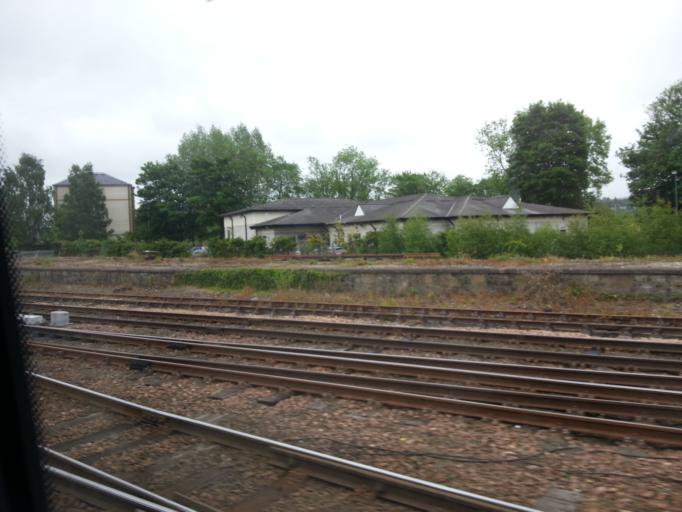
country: GB
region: Scotland
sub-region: Perth and Kinross
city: Perth
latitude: 56.3888
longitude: -3.4376
